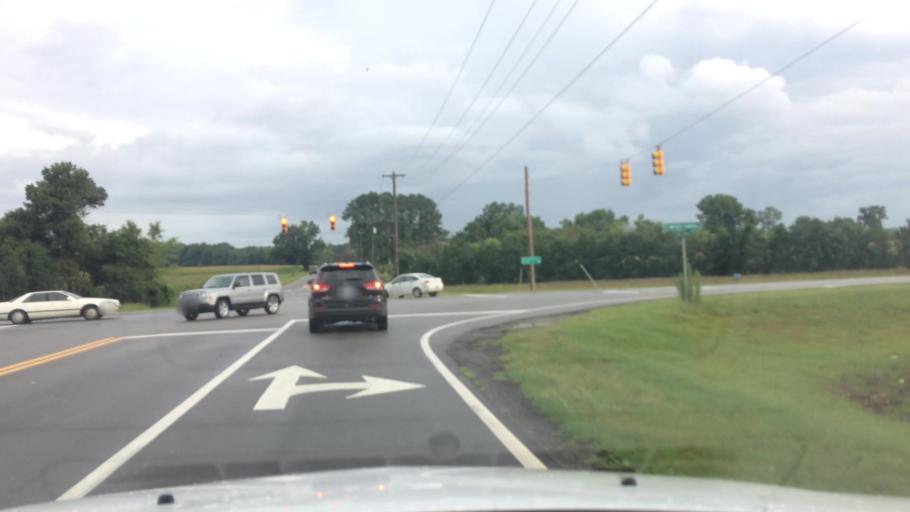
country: US
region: North Carolina
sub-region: Pitt County
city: Farmville
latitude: 35.5848
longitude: -77.5614
